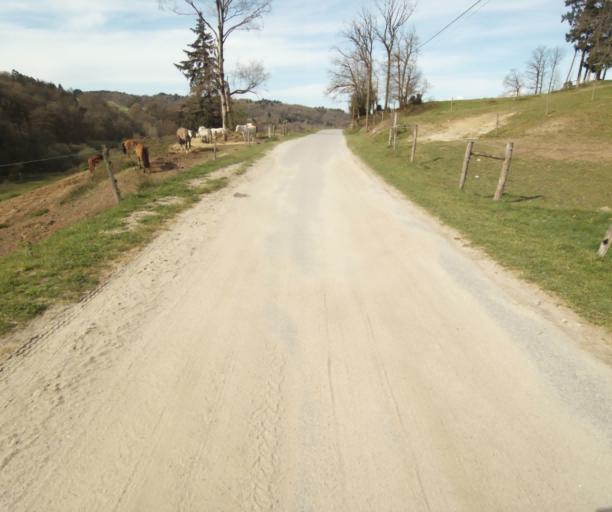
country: FR
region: Limousin
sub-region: Departement de la Correze
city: Correze
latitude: 45.3488
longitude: 1.8671
